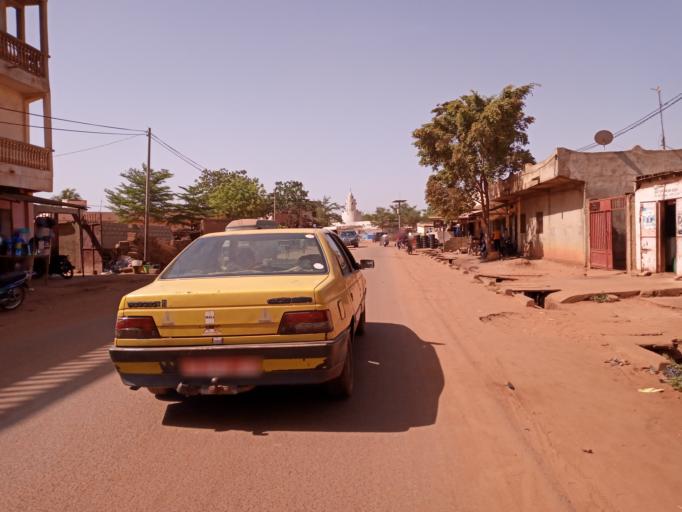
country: ML
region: Bamako
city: Bamako
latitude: 12.5860
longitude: -7.9588
